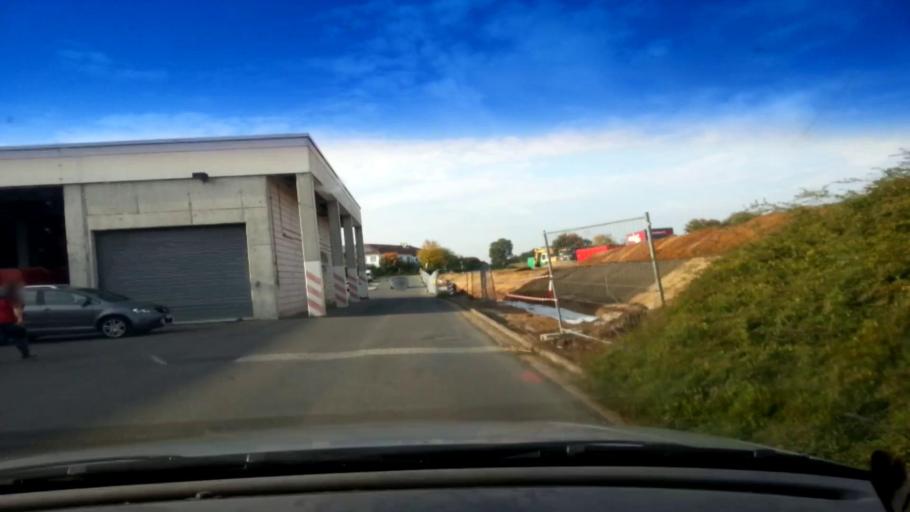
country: DE
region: Bavaria
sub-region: Upper Franconia
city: Hirschaid
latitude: 49.8171
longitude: 11.0055
